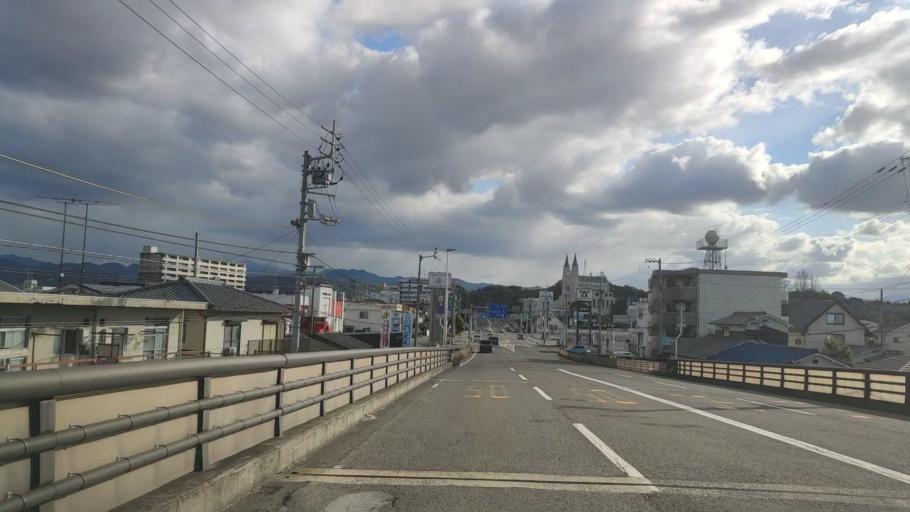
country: JP
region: Ehime
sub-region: Shikoku-chuo Shi
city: Matsuyama
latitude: 33.8570
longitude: 132.7241
